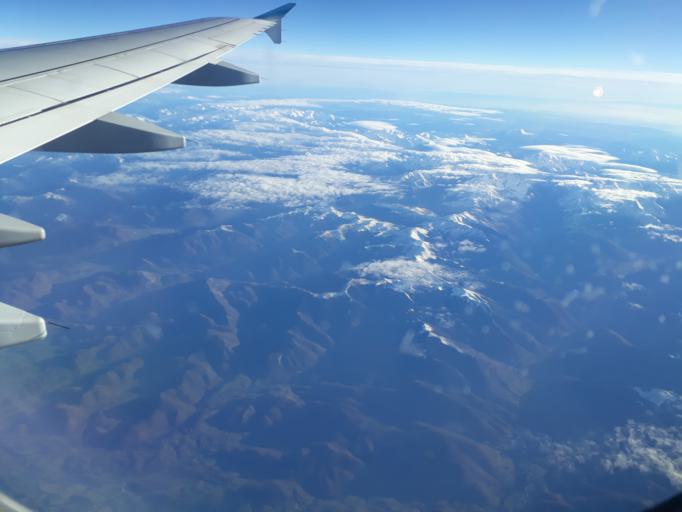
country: FR
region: Midi-Pyrenees
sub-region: Departement des Hautes-Pyrenees
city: Lannemezan
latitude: 43.1305
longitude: 0.3713
